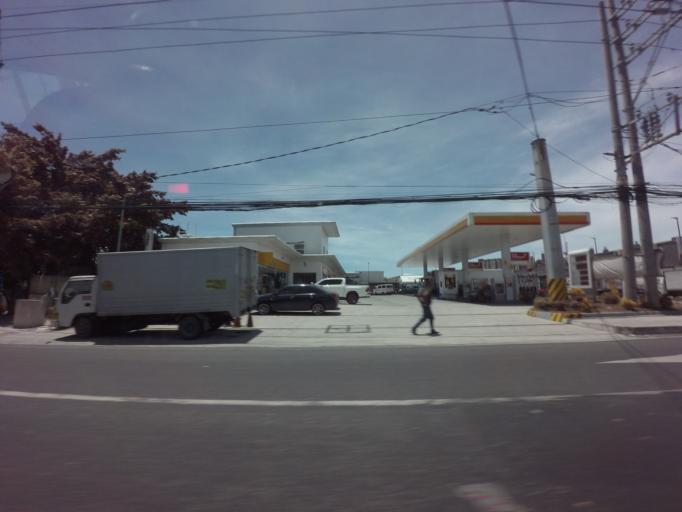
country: PH
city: Sambayanihan People's Village
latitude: 14.4880
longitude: 120.9914
